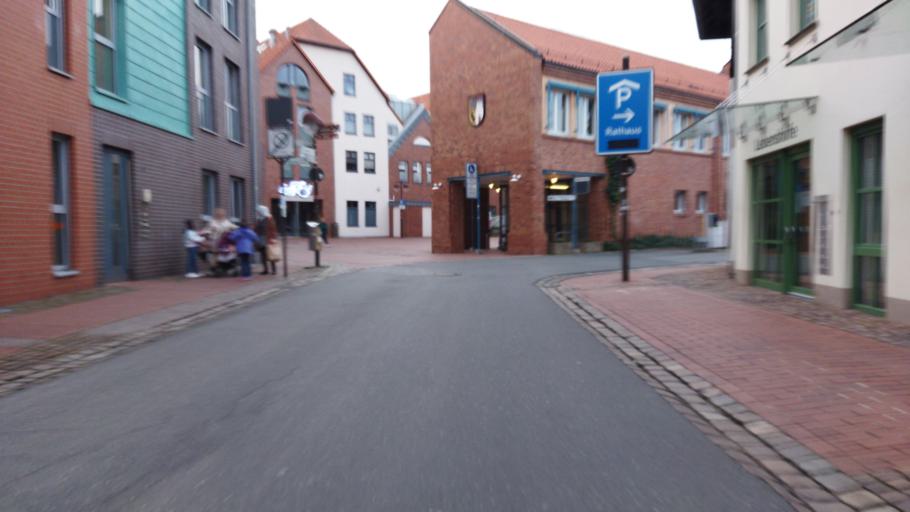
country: DE
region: Lower Saxony
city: Nienburg
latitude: 52.6373
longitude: 9.2052
